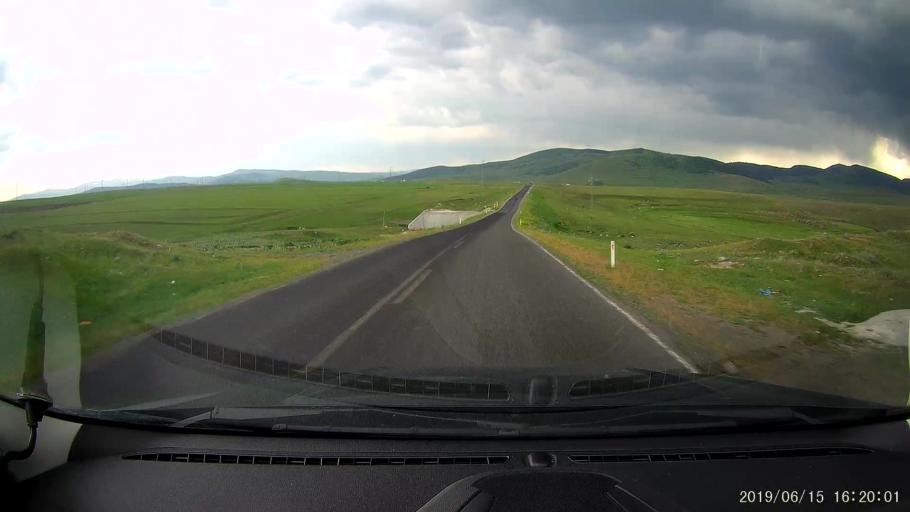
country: TR
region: Ardahan
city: Hanak
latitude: 41.2203
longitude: 42.8497
